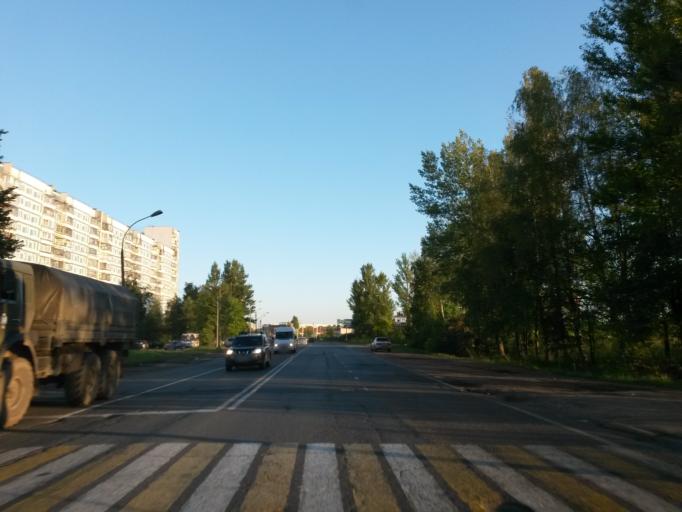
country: RU
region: Jaroslavl
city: Yaroslavl
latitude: 57.7050
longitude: 39.7591
